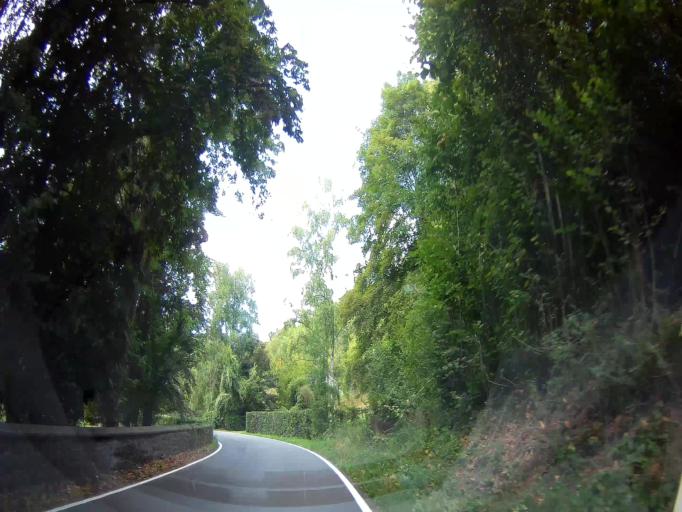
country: BE
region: Wallonia
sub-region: Province de Namur
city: Onhaye
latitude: 50.2917
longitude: 4.8127
